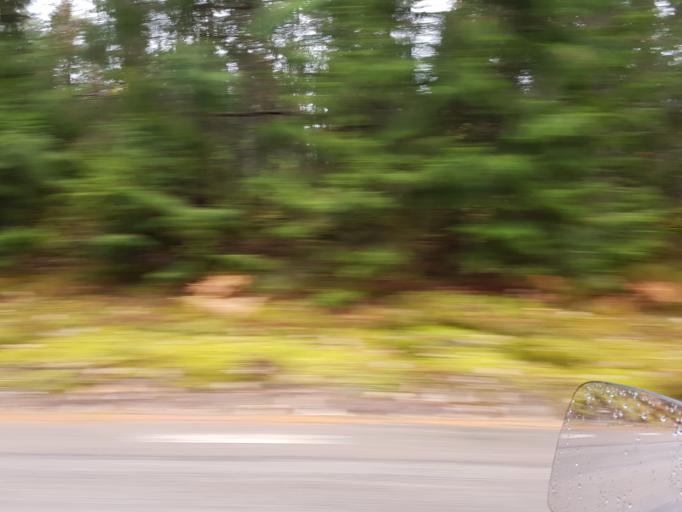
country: SE
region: Vaestra Goetaland
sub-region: Orust
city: Henan
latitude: 58.2731
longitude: 11.7212
